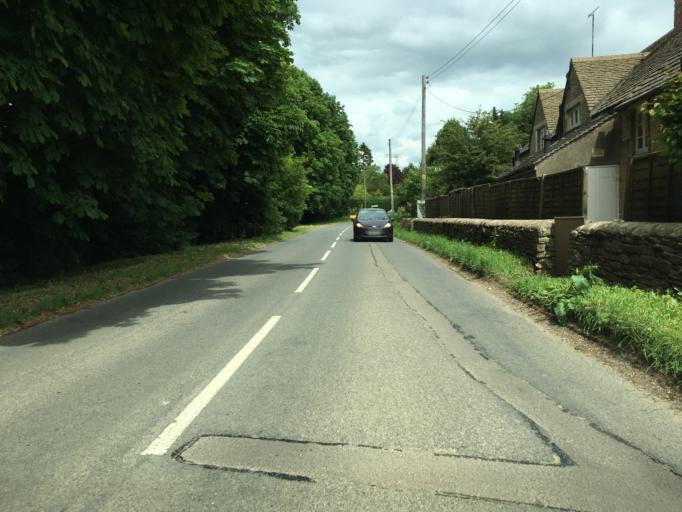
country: GB
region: England
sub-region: Gloucestershire
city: Cirencester
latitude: 51.6772
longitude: -1.9917
